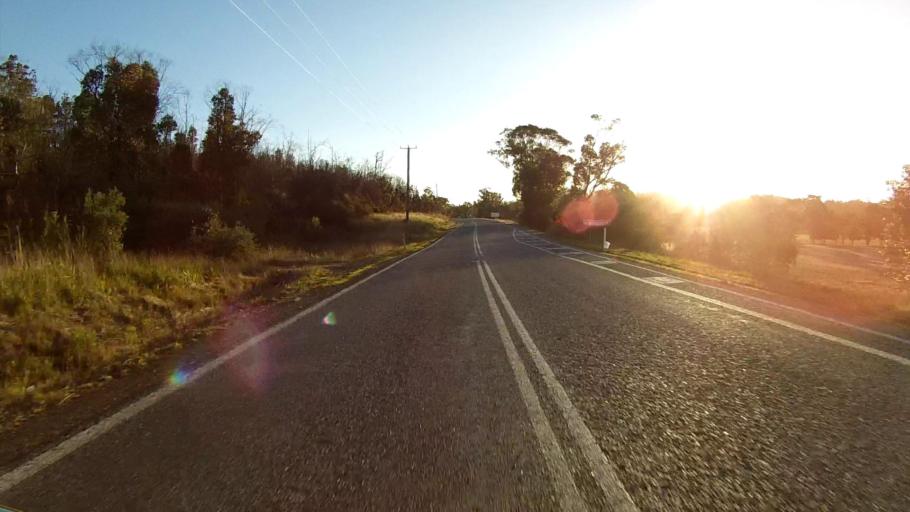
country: AU
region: Tasmania
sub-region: Sorell
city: Sorell
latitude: -42.8230
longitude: 147.6959
